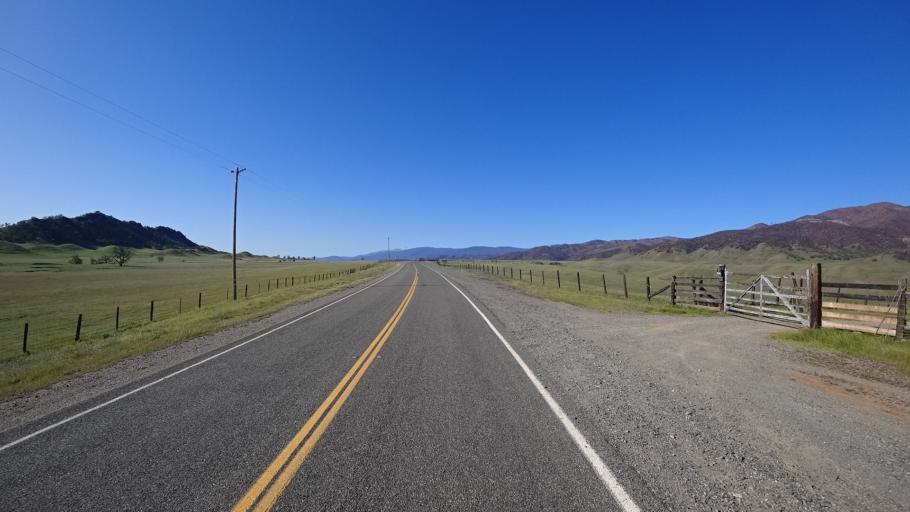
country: US
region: California
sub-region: Tehama County
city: Rancho Tehama Reserve
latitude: 39.7446
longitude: -122.5418
